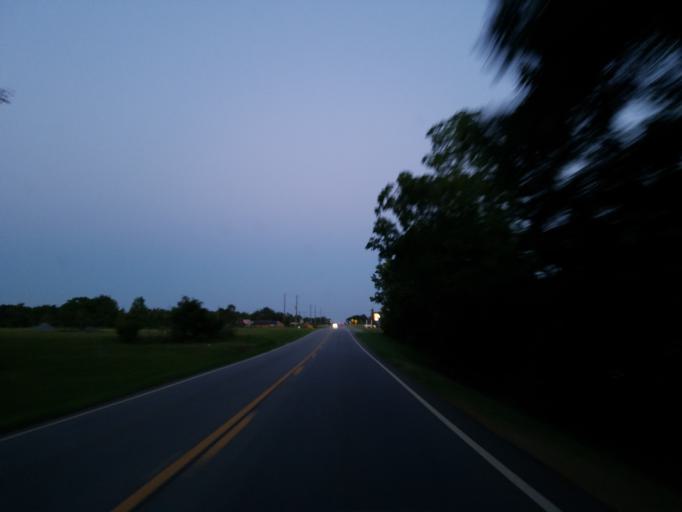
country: US
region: Georgia
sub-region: Dooly County
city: Unadilla
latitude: 32.3379
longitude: -83.7719
